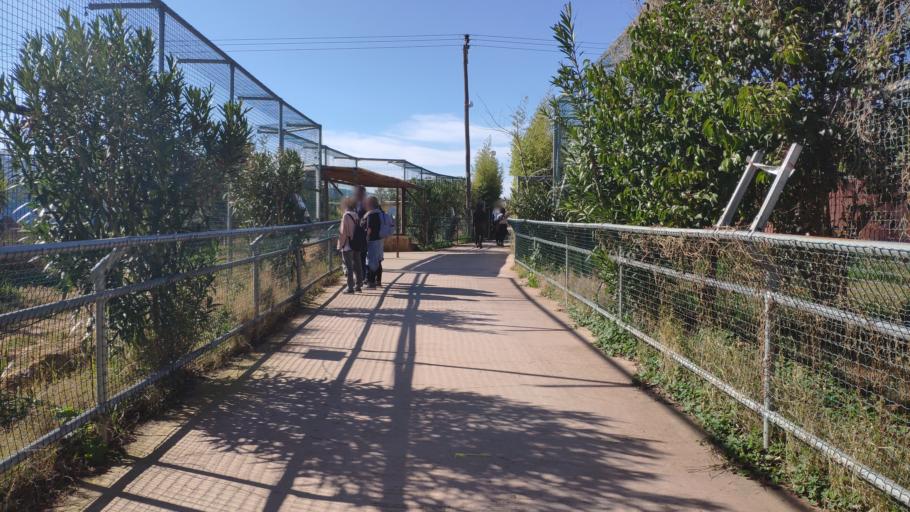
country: GR
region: Attica
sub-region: Nomarchia Anatolikis Attikis
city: Spata
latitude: 37.9791
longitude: 23.9092
